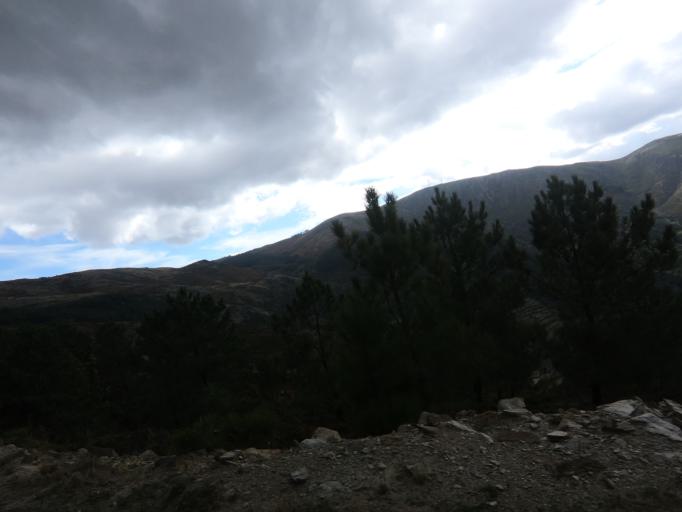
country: PT
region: Vila Real
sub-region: Mondim de Basto
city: Mondim de Basto
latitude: 41.3708
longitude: -7.8420
